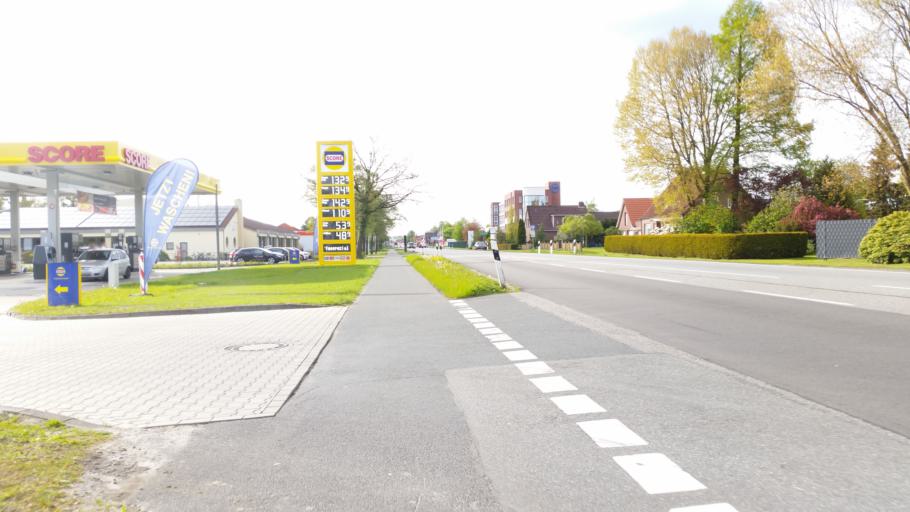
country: DE
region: Lower Saxony
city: Aurich
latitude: 53.4587
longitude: 7.4949
